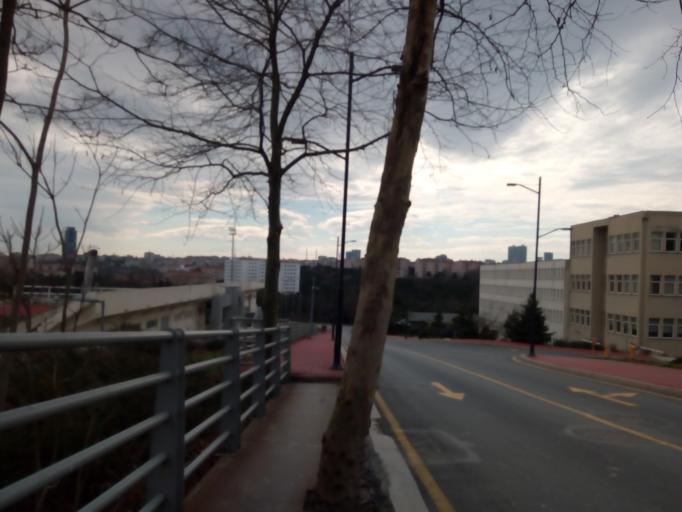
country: TR
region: Istanbul
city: Sisli
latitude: 41.1022
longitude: 29.0222
